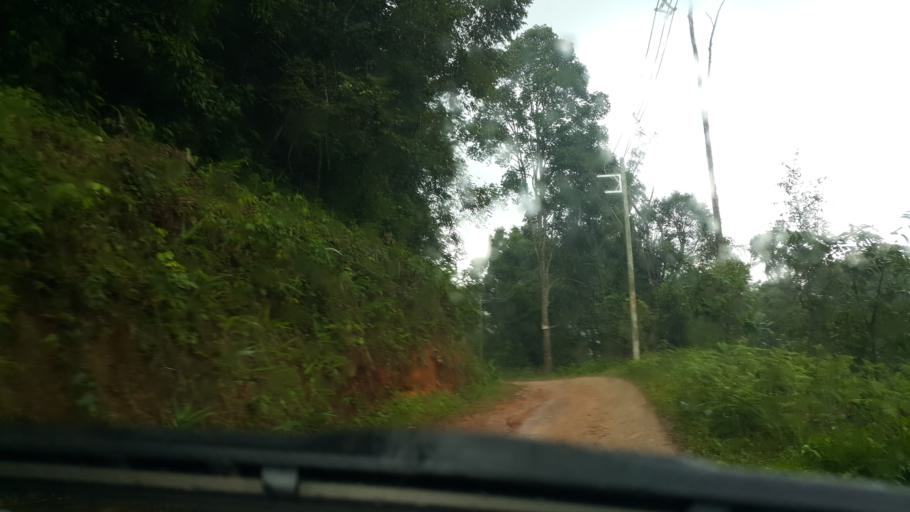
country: TH
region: Lampang
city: Wang Nuea
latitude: 19.1264
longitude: 99.3629
